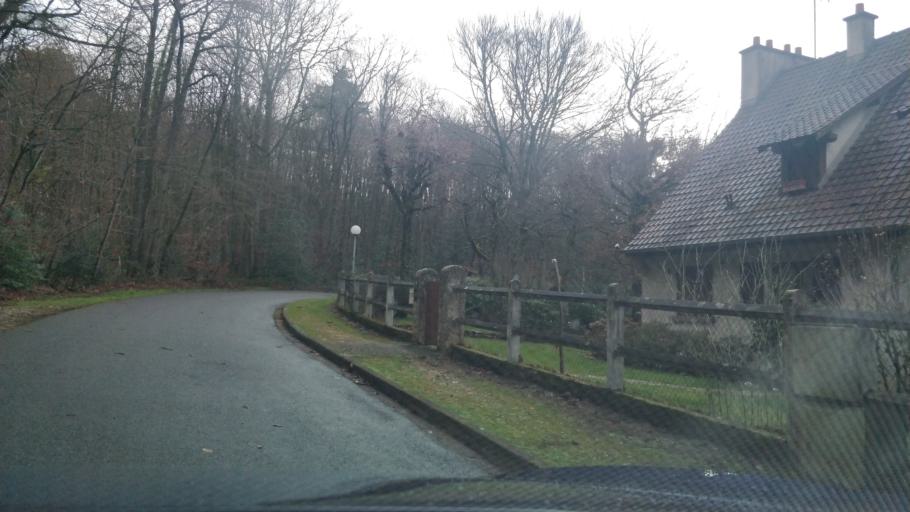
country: FR
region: Ile-de-France
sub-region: Departement de l'Essonne
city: Briis-sous-Forges
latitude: 48.6330
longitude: 2.1221
